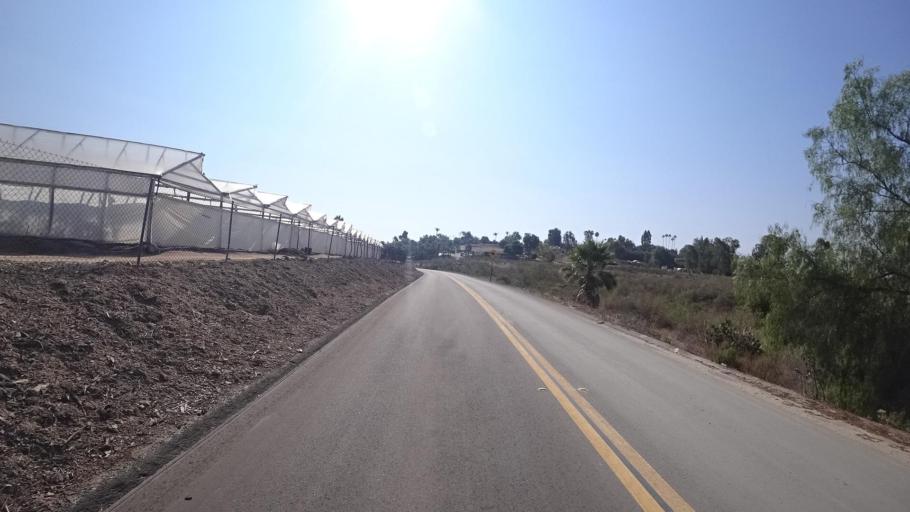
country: US
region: California
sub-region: San Diego County
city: Vista
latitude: 33.2415
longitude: -117.2622
